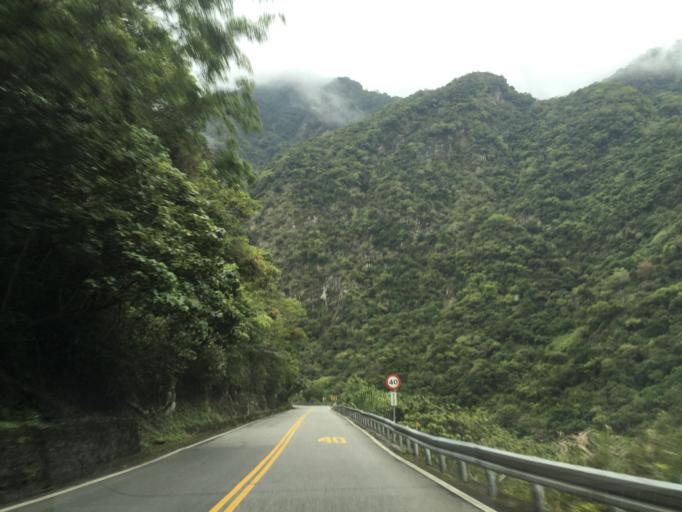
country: TW
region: Taiwan
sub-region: Hualien
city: Hualian
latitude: 24.1739
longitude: 121.5872
